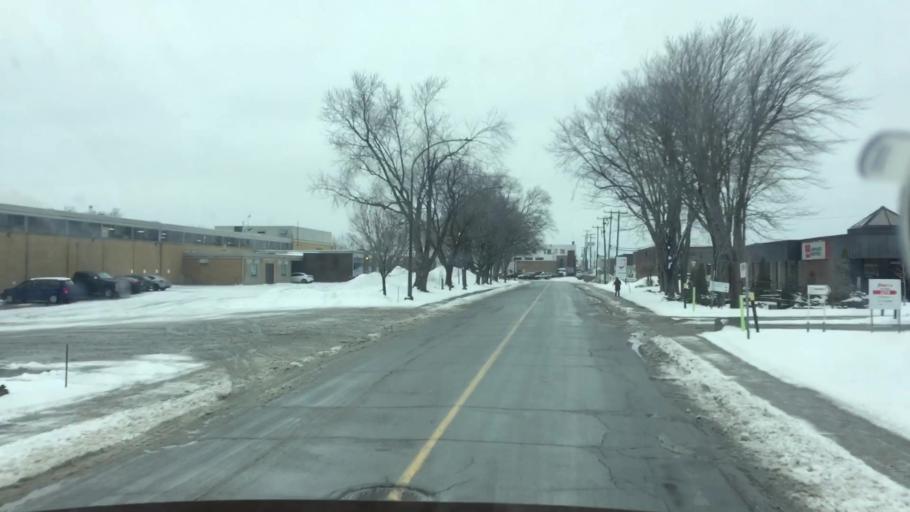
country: CA
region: Quebec
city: Dorval
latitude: 45.4588
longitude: -73.7206
